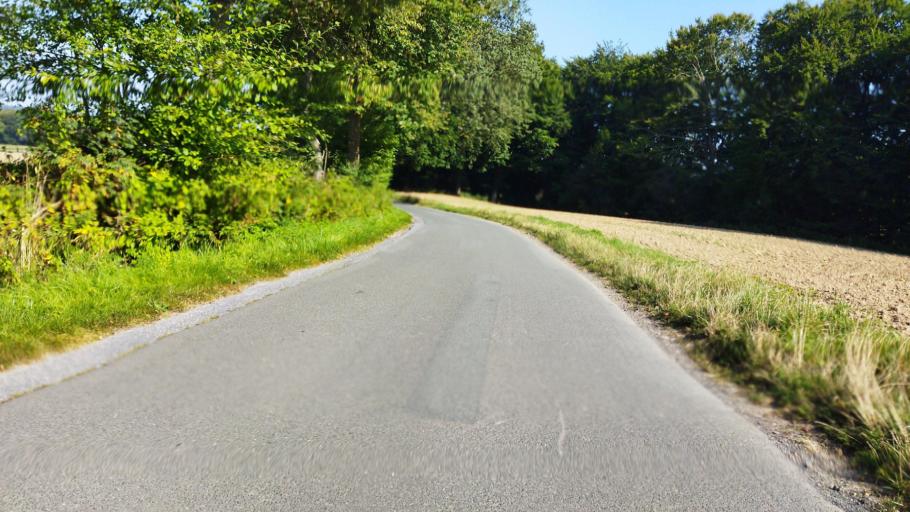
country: DE
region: North Rhine-Westphalia
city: Lengerich
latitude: 52.2242
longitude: 7.8611
